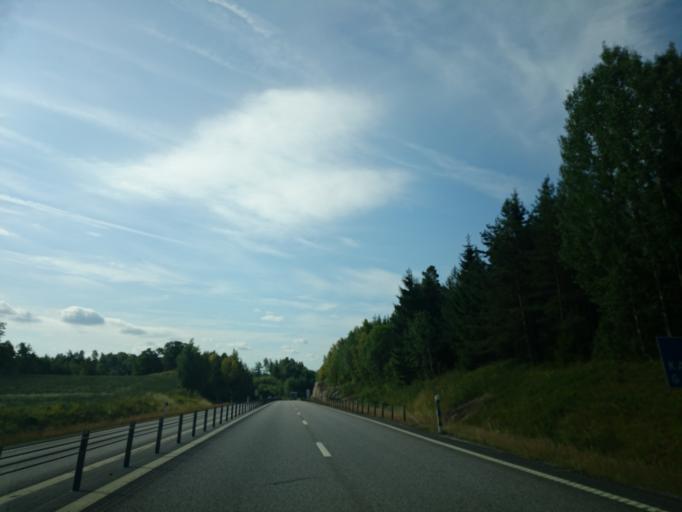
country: SE
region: OEstergoetland
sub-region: Valdemarsviks Kommun
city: Valdemarsvik
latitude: 58.2176
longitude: 16.5551
